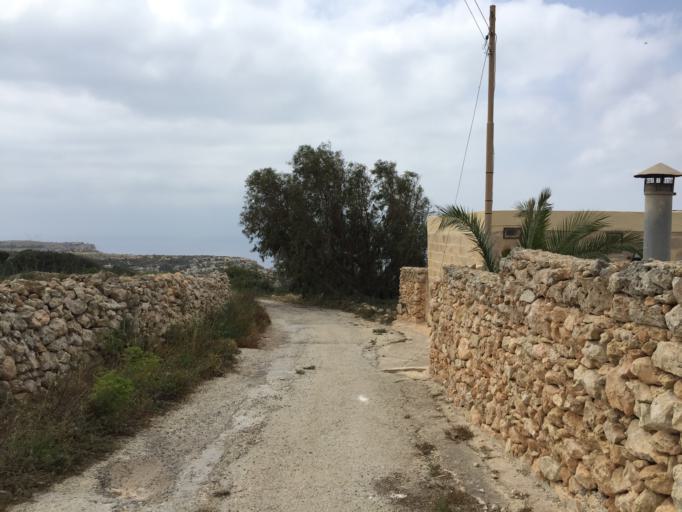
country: MT
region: L-Imgarr
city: Imgarr
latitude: 35.9018
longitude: 14.3474
